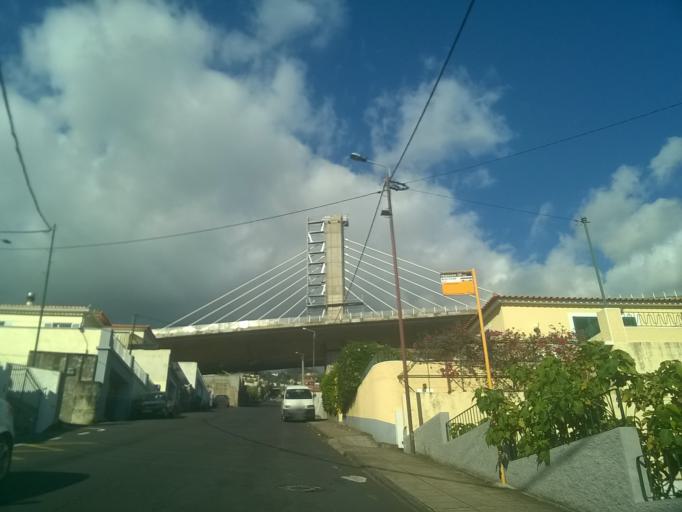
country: PT
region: Madeira
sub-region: Funchal
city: Nossa Senhora do Monte
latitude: 32.6618
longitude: -16.9079
